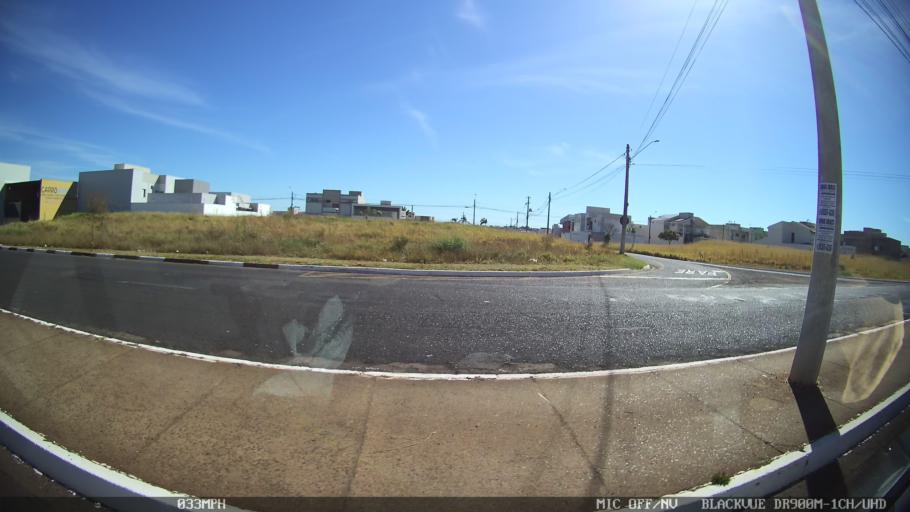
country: BR
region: Sao Paulo
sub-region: Franca
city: Franca
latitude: -20.5408
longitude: -47.3704
